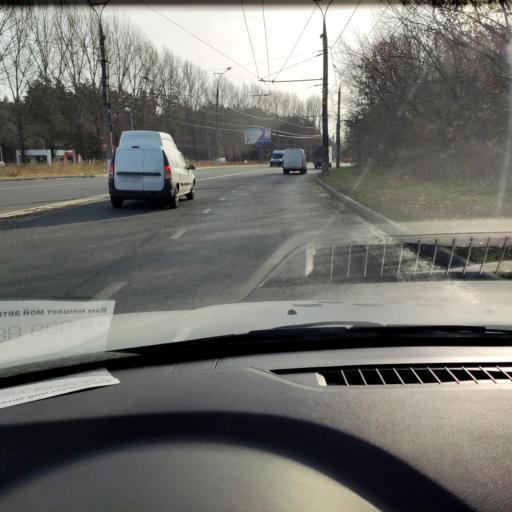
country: RU
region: Samara
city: Zhigulevsk
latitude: 53.5095
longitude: 49.4622
